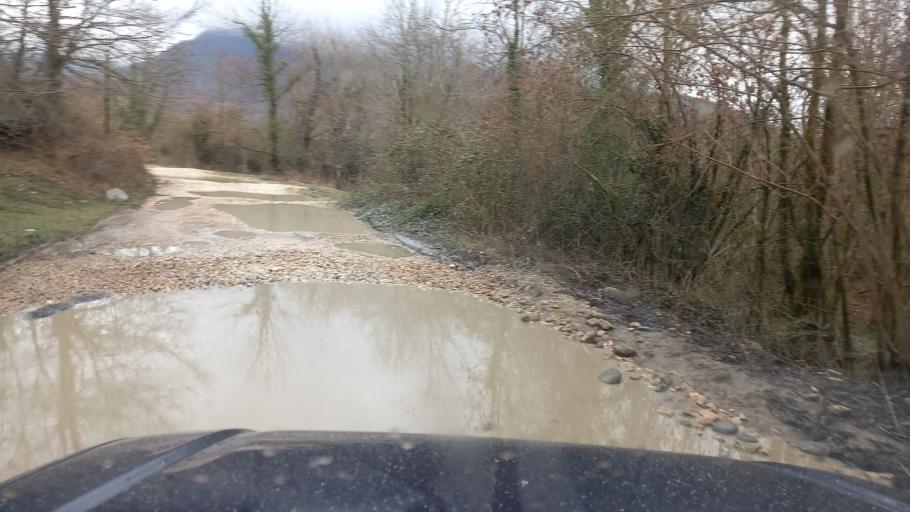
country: GE
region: Abkhazia
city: Dranda
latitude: 43.0342
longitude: 41.3232
